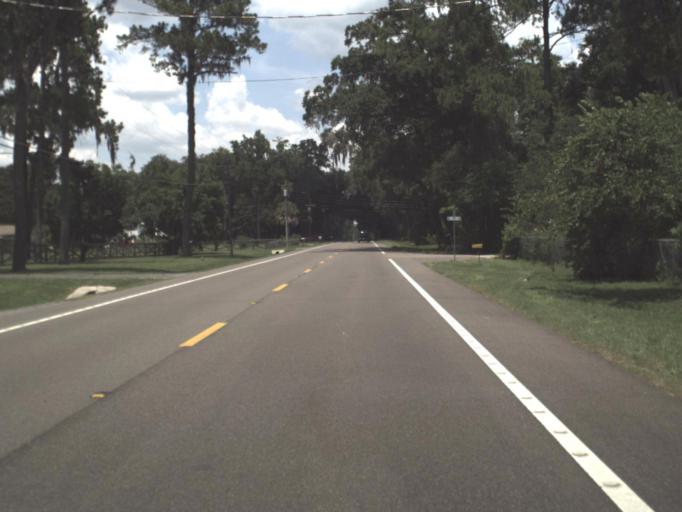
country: US
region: Florida
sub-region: Alachua County
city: Gainesville
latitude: 29.6697
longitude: -82.2453
